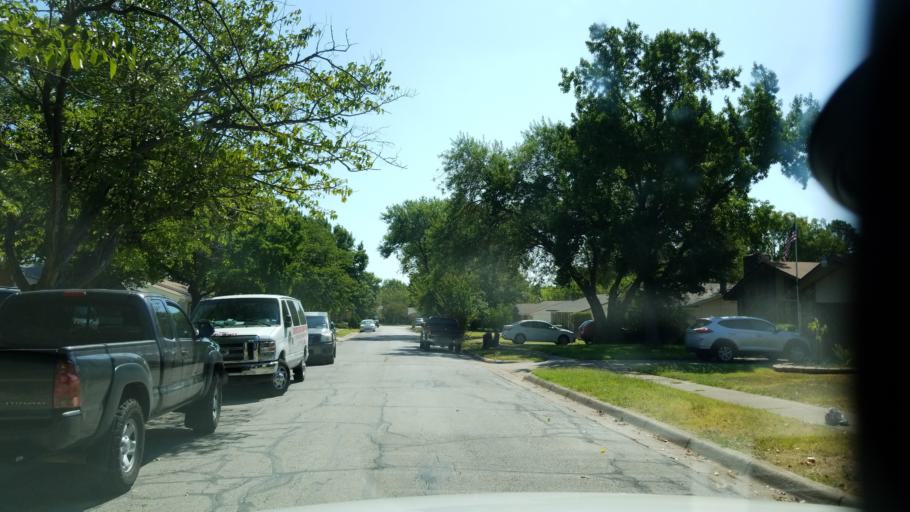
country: US
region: Texas
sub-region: Dallas County
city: Duncanville
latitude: 32.6429
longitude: -96.9006
